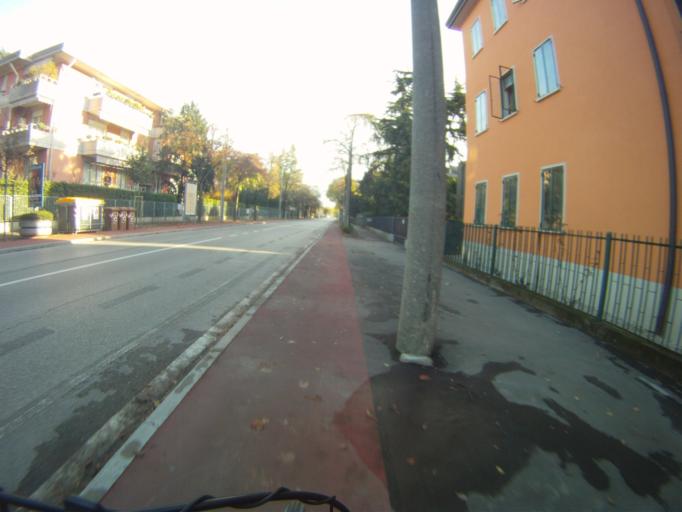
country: IT
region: Veneto
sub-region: Provincia di Padova
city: Padova
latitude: 45.3879
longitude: 11.8955
